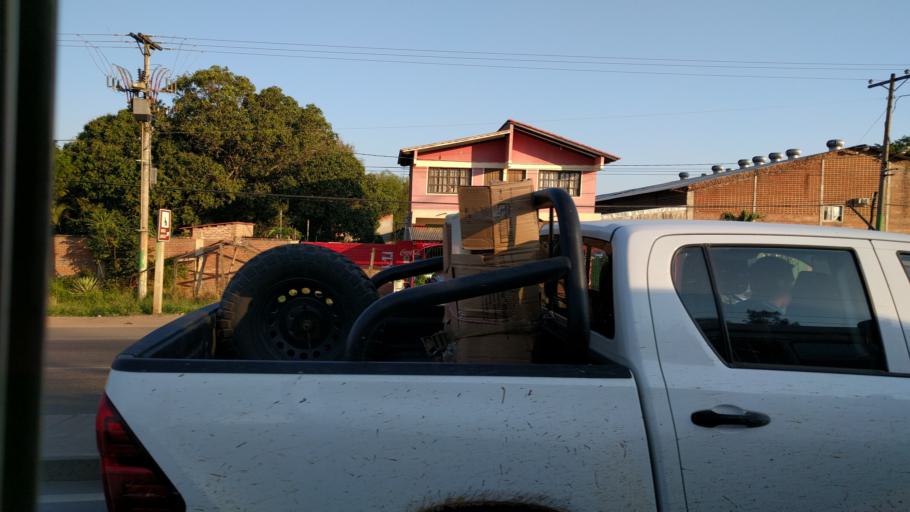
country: BO
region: Santa Cruz
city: Cotoca
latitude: -17.7597
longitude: -63.0156
